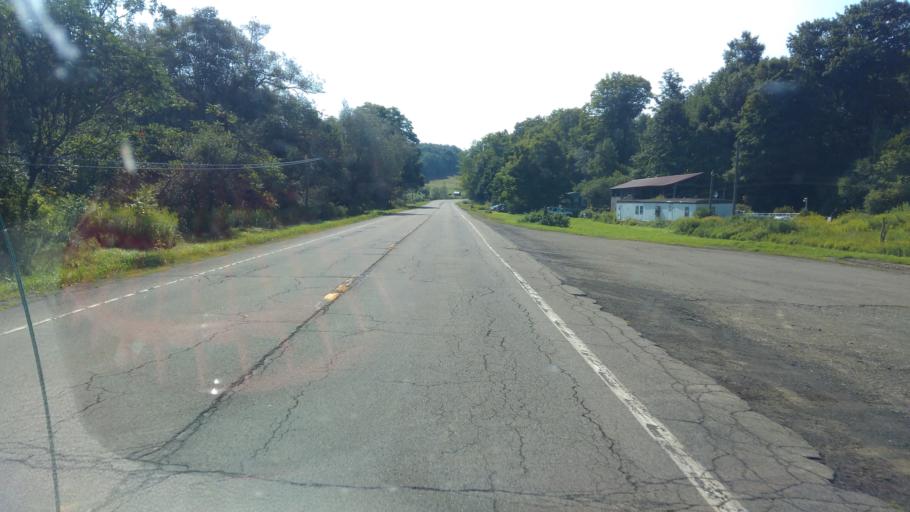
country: US
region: New York
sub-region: Allegany County
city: Cuba
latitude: 42.1852
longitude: -78.2599
